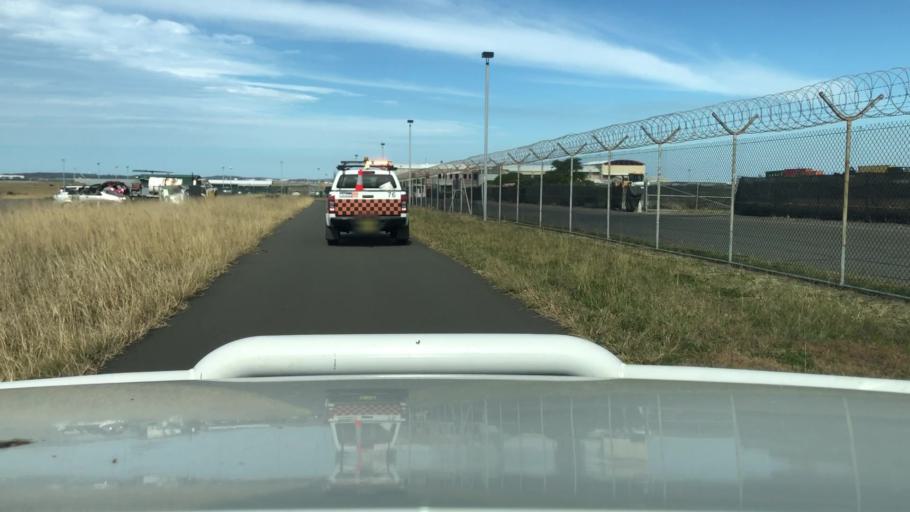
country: AU
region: New South Wales
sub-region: Botany Bay
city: Botany
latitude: -33.9470
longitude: 151.1853
